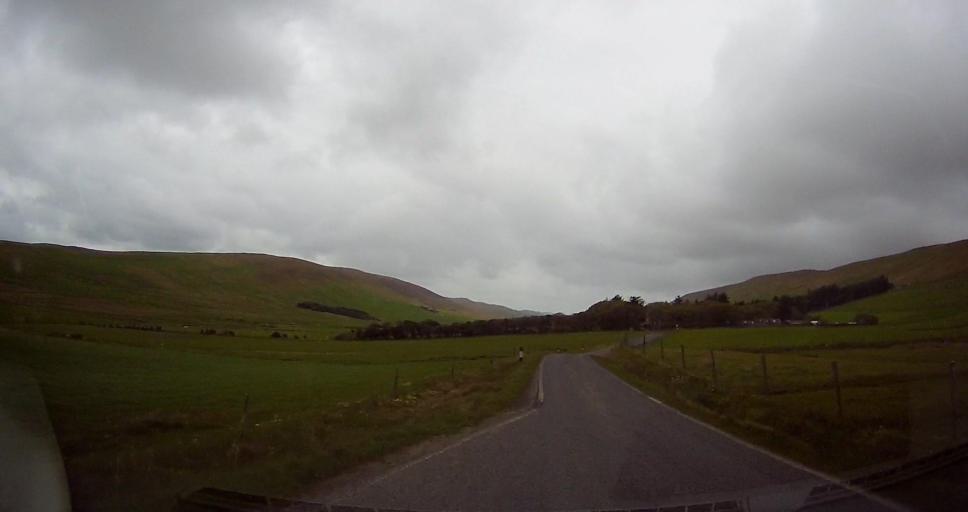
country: GB
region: Scotland
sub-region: Shetland Islands
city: Lerwick
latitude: 60.2743
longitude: -1.2845
